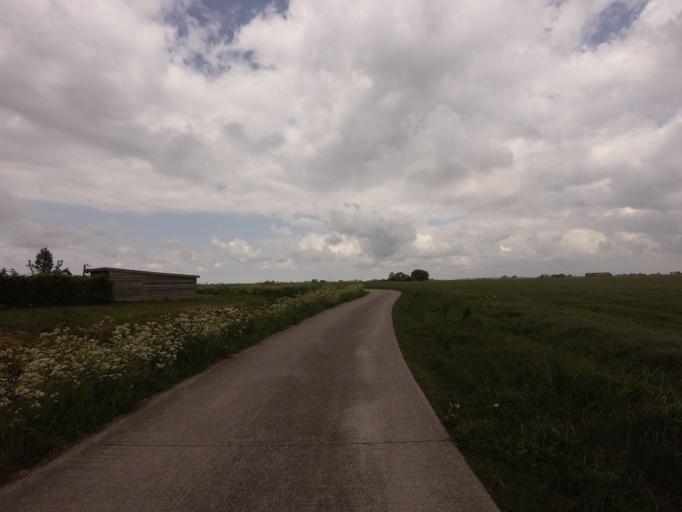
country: NL
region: Friesland
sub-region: Gemeente Littenseradiel
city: Wommels
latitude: 53.1083
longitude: 5.5987
